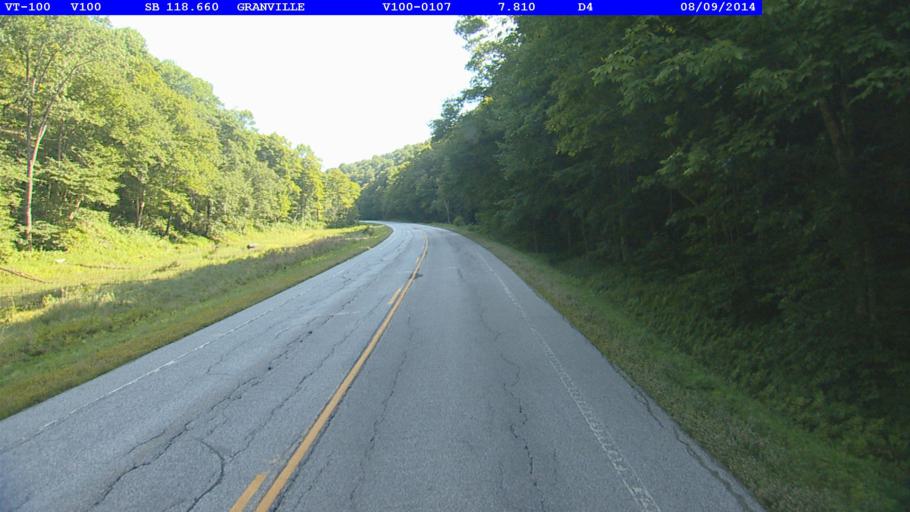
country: US
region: Vermont
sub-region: Orange County
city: Randolph
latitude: 44.0425
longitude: -72.8322
